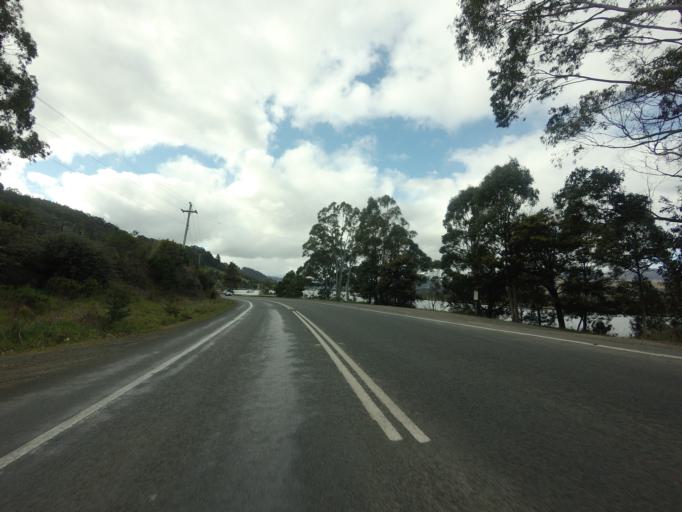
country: AU
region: Tasmania
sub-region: Huon Valley
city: Franklin
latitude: -43.1092
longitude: 147.0004
